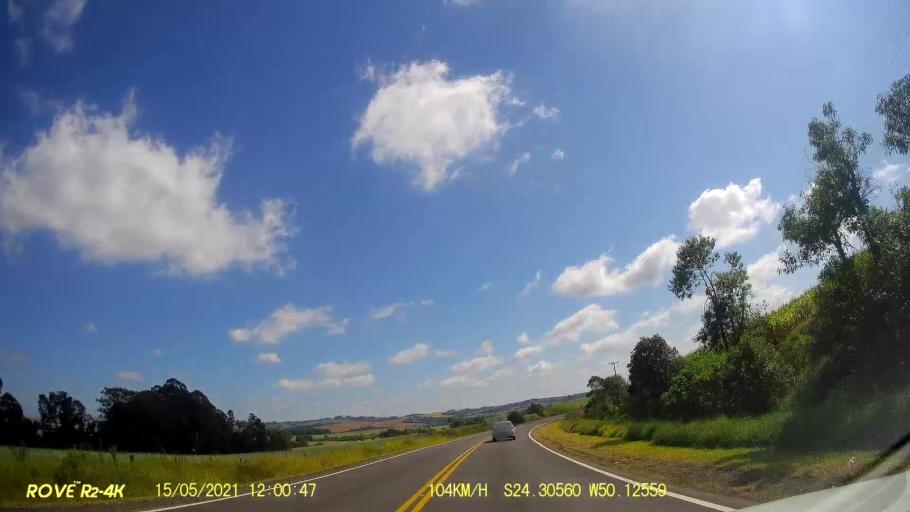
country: BR
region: Parana
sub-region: Pirai Do Sul
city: Pirai do Sul
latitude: -24.3057
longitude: -50.1254
